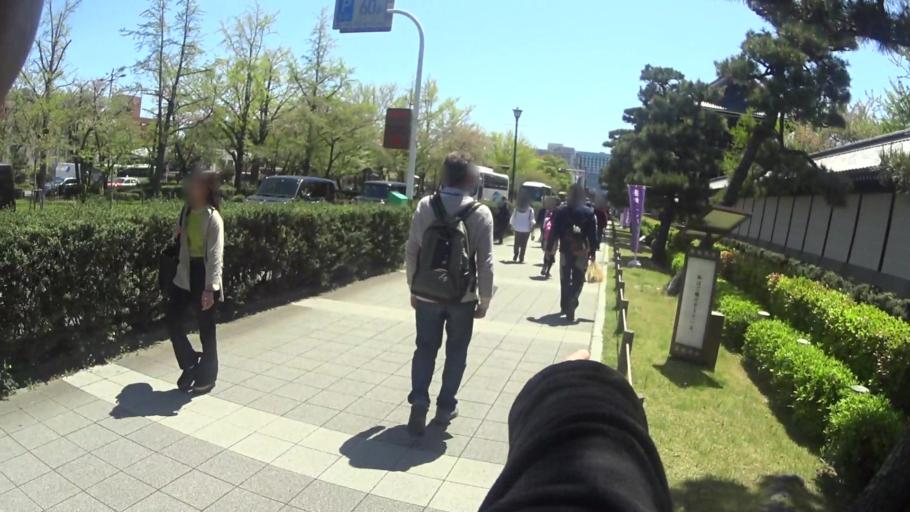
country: JP
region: Kyoto
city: Kyoto
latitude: 34.9919
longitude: 135.7596
